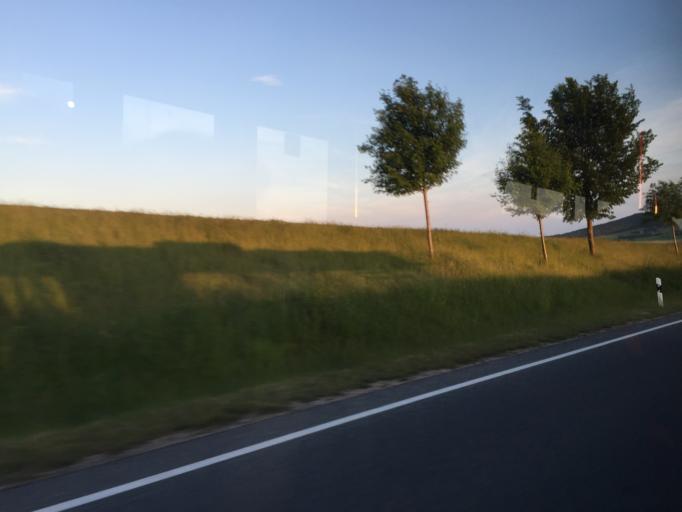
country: DE
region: Saxony
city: Reichenbach
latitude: 51.1440
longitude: 14.7740
